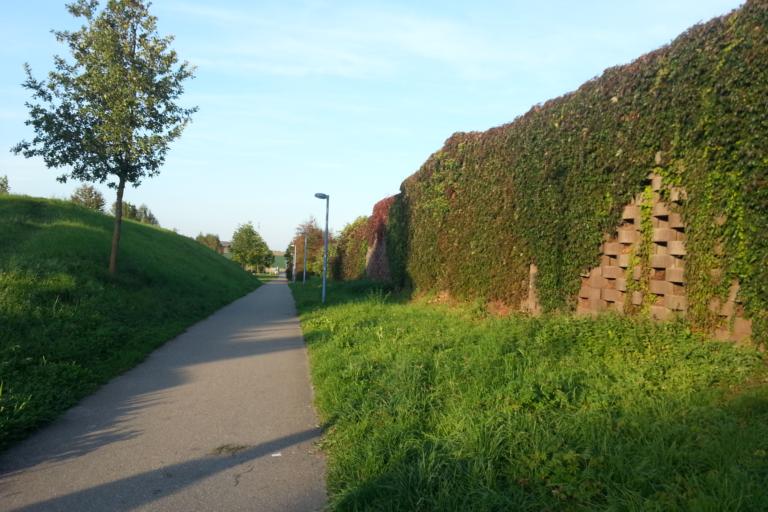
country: DE
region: Baden-Wuerttemberg
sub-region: Regierungsbezirk Stuttgart
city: Gartringen
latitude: 48.6445
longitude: 8.9128
